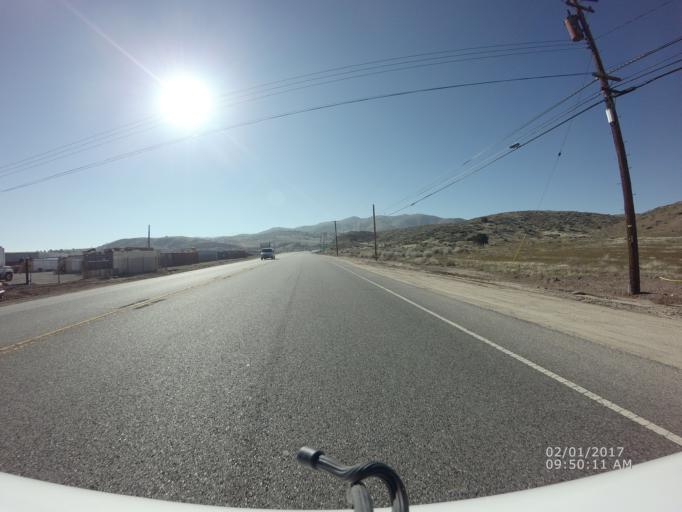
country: US
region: California
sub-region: Los Angeles County
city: Vincent
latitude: 34.5254
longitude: -118.0985
